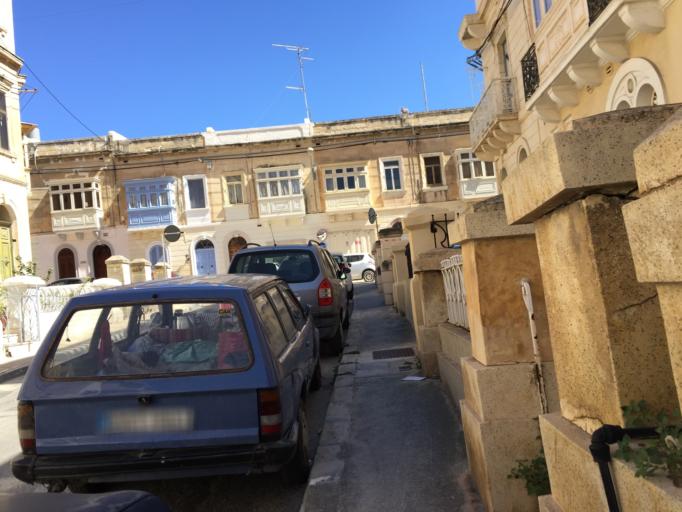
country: MT
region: Tas-Sliema
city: Sliema
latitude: 35.9123
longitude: 14.4966
